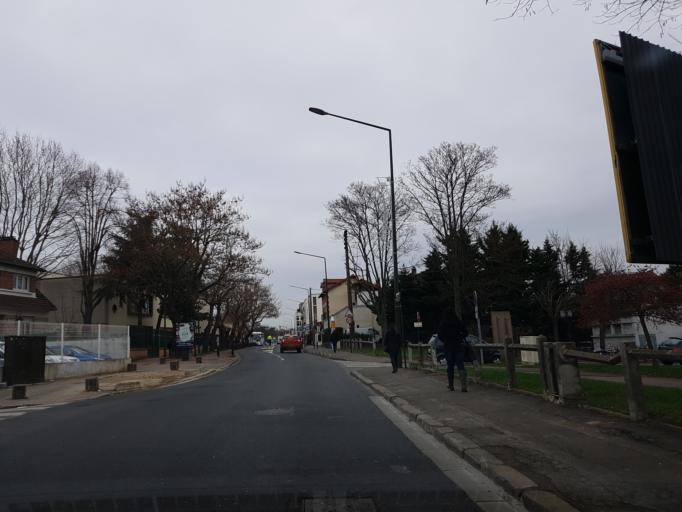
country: FR
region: Ile-de-France
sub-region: Departement du Val-de-Marne
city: Villejuif
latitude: 48.7853
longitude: 2.3545
